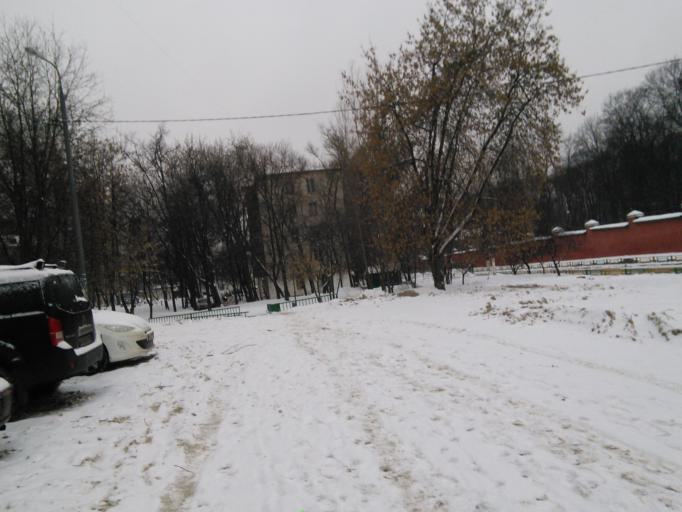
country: RU
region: Moscow
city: Lefortovo
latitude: 55.7676
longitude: 37.7110
